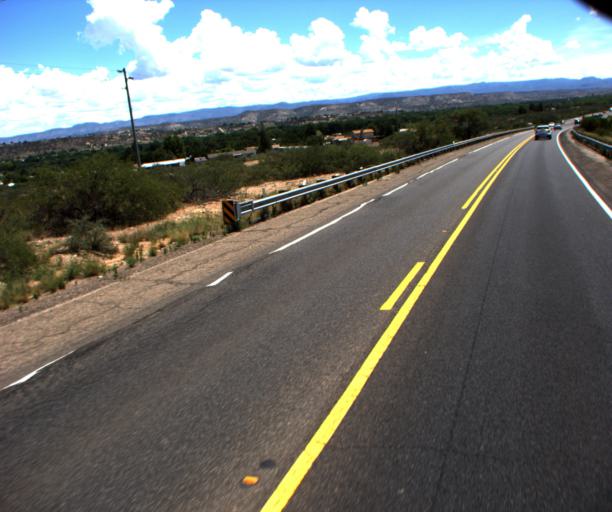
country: US
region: Arizona
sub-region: Yavapai County
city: Camp Verde
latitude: 34.5974
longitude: -111.8954
